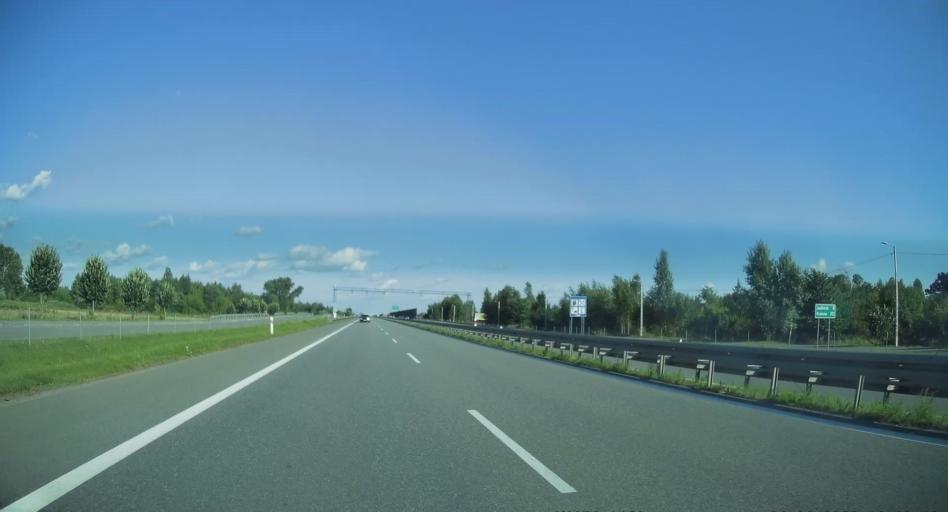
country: PL
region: Masovian Voivodeship
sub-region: Powiat bialobrzeski
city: Stara Blotnica
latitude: 51.5565
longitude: 21.0320
